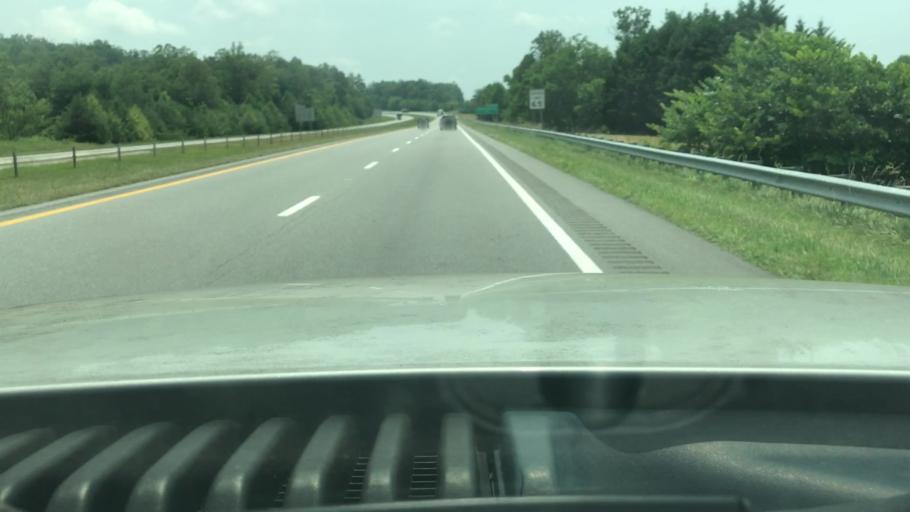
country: US
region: North Carolina
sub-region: Yadkin County
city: Jonesville
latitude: 36.1496
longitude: -80.9211
